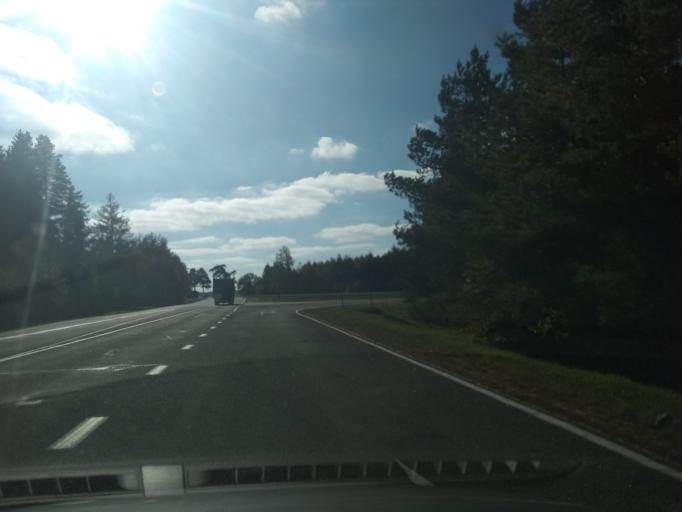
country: BY
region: Minsk
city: Haradzyeya
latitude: 53.3774
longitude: 26.5099
